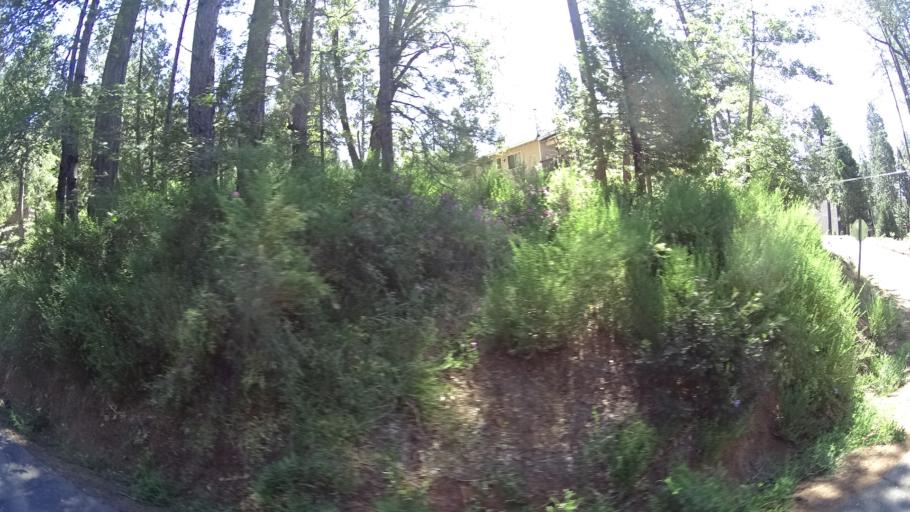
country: US
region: California
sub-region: Calaveras County
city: Arnold
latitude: 38.2379
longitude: -120.3752
